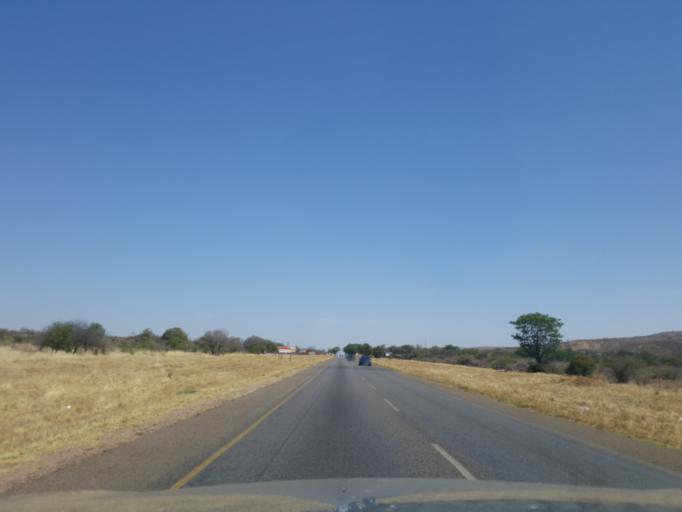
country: BW
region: South East
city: Lobatse
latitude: -25.1650
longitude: 25.6877
